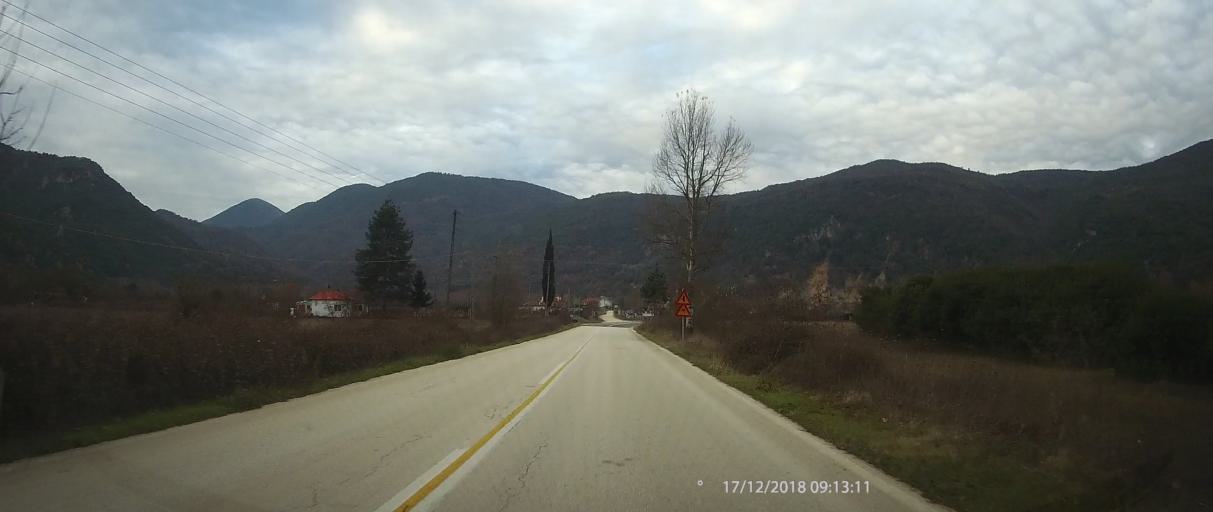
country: GR
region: Epirus
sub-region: Nomos Ioanninon
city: Kalpaki
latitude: 39.9746
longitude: 20.6613
